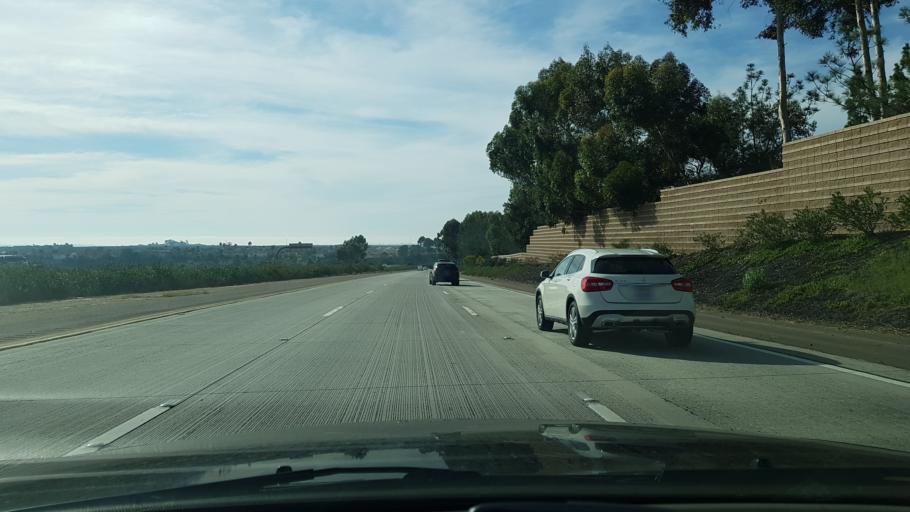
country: US
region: California
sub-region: San Diego County
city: Fairbanks Ranch
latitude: 32.9535
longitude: -117.1373
